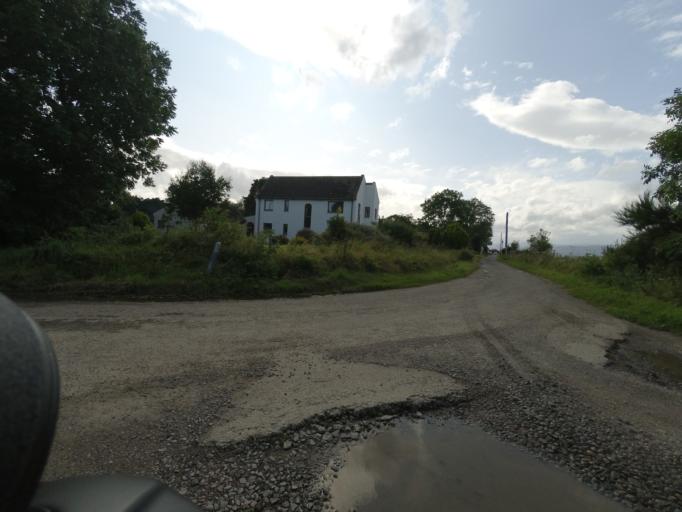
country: GB
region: Scotland
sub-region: Highland
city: Invergordon
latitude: 57.6756
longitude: -4.1657
